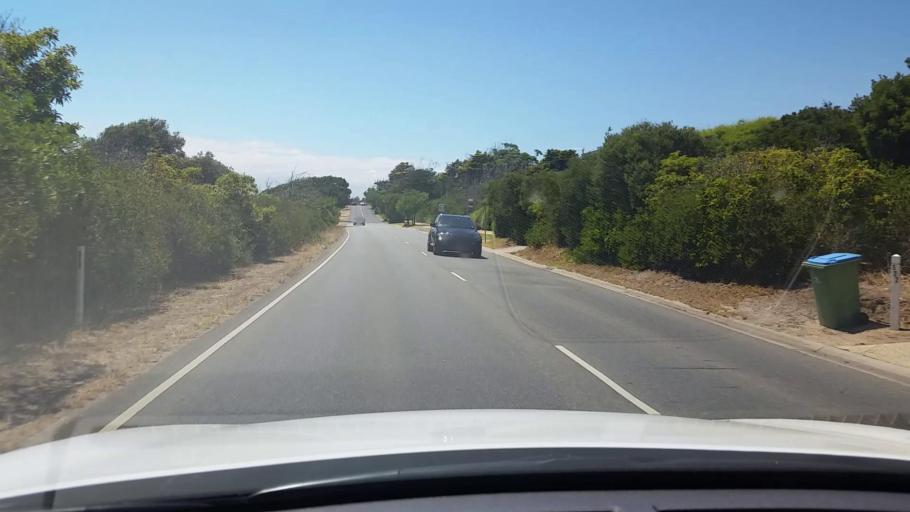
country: AU
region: Victoria
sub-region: Mornington Peninsula
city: Mount Martha
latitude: -38.2607
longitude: 145.0199
